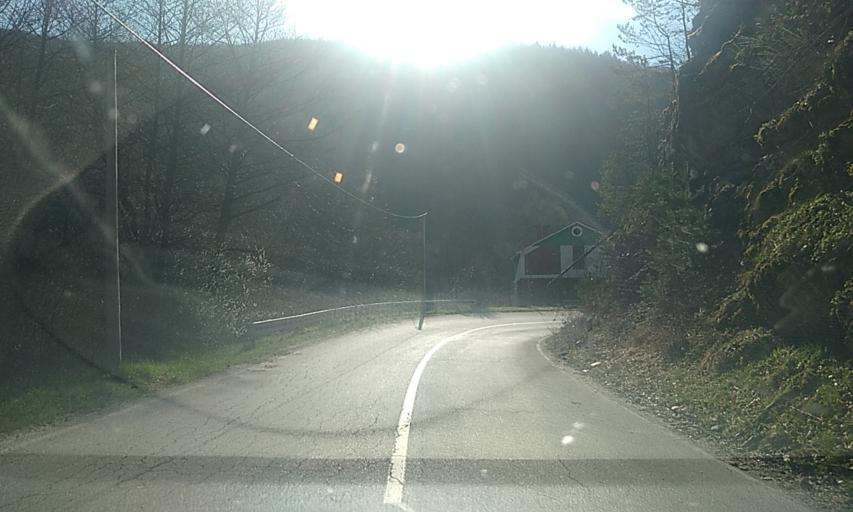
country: RS
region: Central Serbia
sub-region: Pcinjski Okrug
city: Bosilegrad
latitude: 42.4241
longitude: 22.5230
